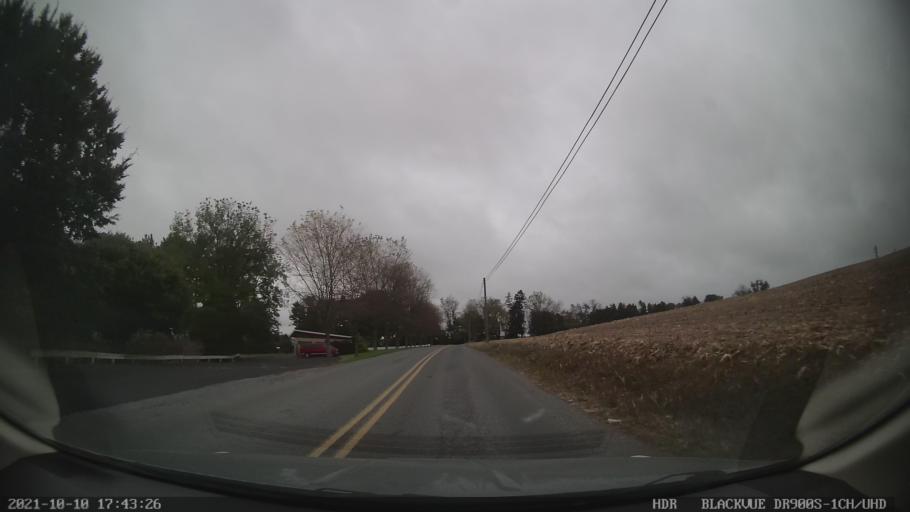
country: US
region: Pennsylvania
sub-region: Berks County
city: Topton
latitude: 40.5368
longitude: -75.6771
